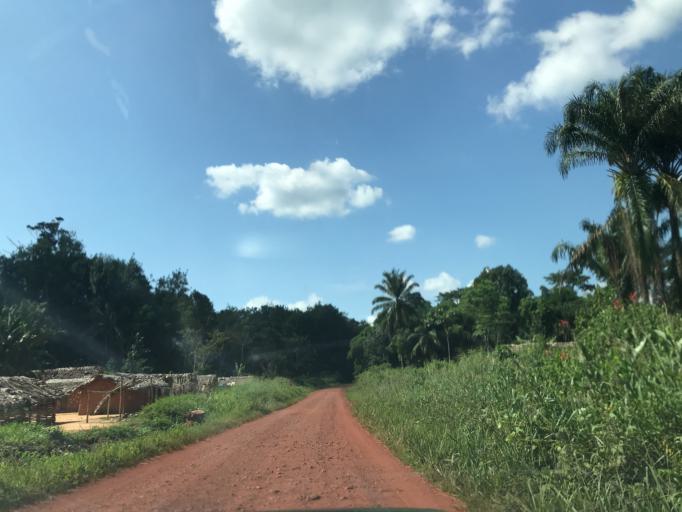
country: CD
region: Eastern Province
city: Kisangani
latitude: 1.2261
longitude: 25.2681
